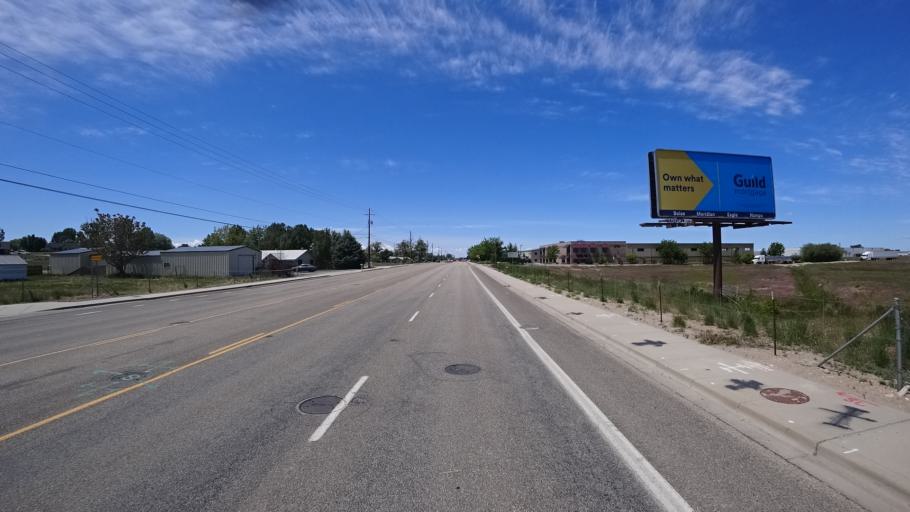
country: US
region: Idaho
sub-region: Ada County
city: Garden City
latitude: 43.5756
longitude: -116.2636
